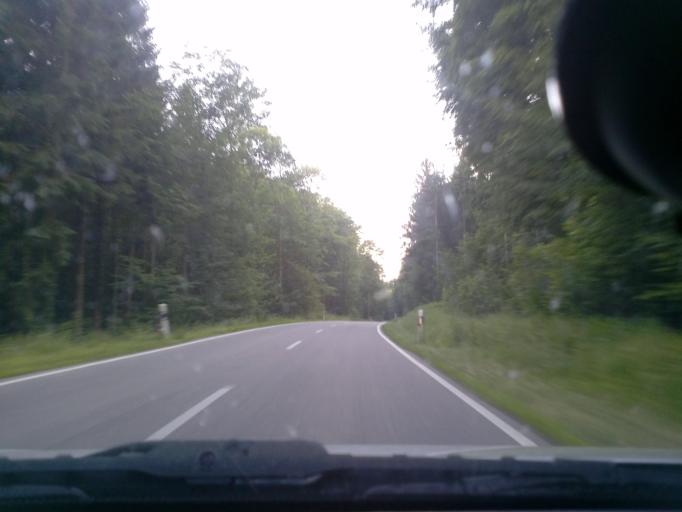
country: DE
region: Baden-Wuerttemberg
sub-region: Karlsruhe Region
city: Eisingen
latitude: 48.9973
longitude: 8.6598
